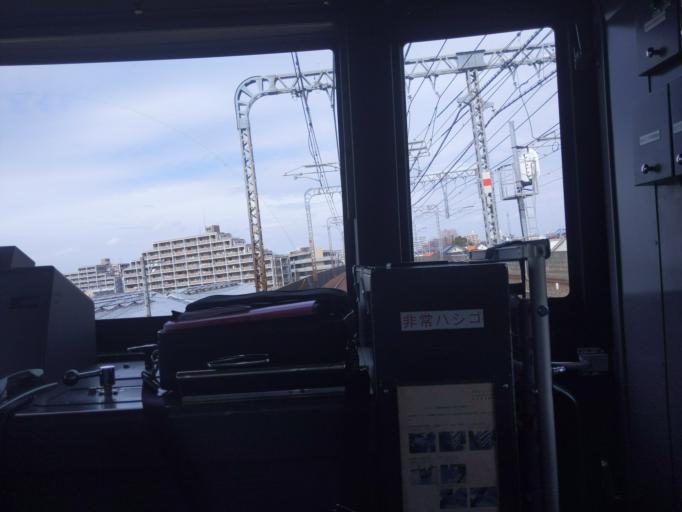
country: JP
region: Saitama
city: Koshigaya
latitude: 35.8572
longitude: 139.7939
